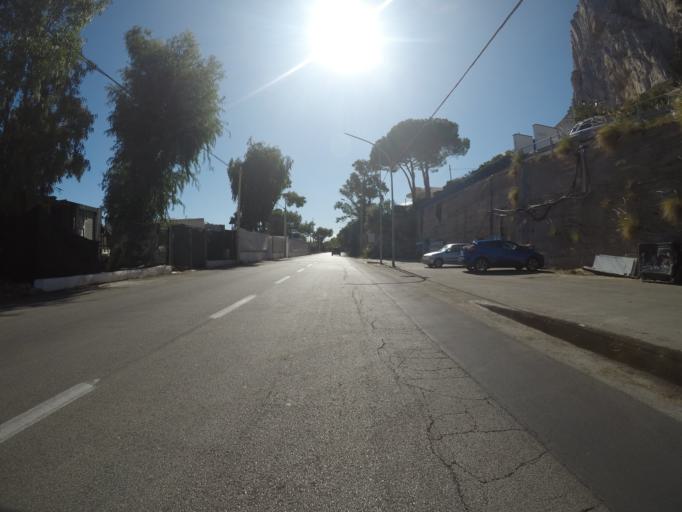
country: IT
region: Sicily
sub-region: Palermo
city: Palermo
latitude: 38.1843
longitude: 13.3632
